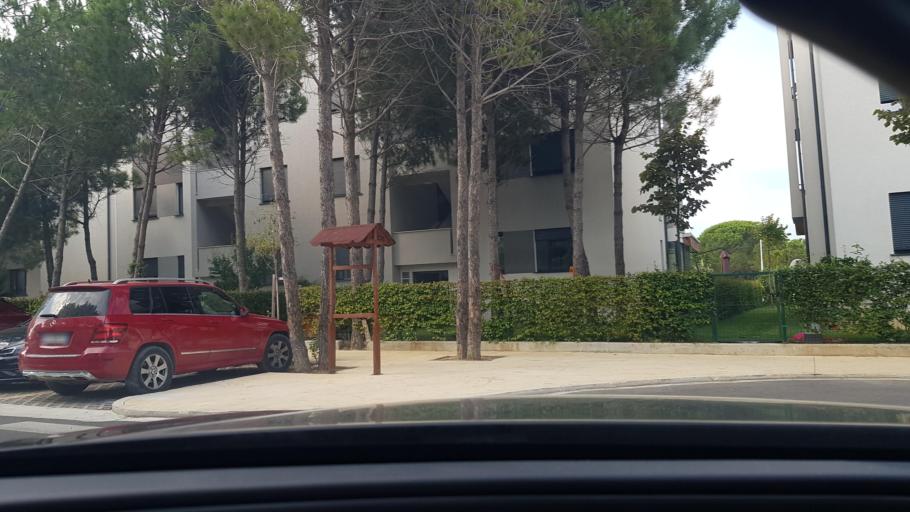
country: AL
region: Durres
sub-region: Rrethi i Durresit
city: Katundi i Ri
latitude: 41.4956
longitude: 19.5154
